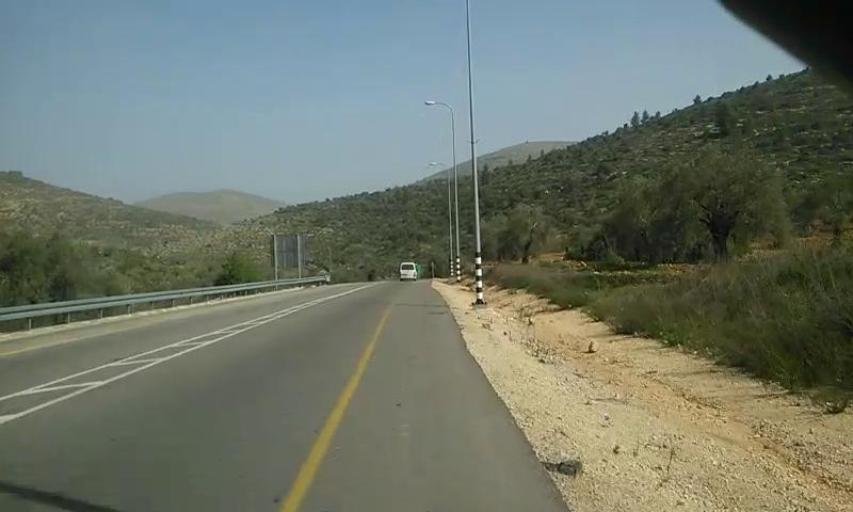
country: PS
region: West Bank
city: `Atarah
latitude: 31.9922
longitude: 35.2281
